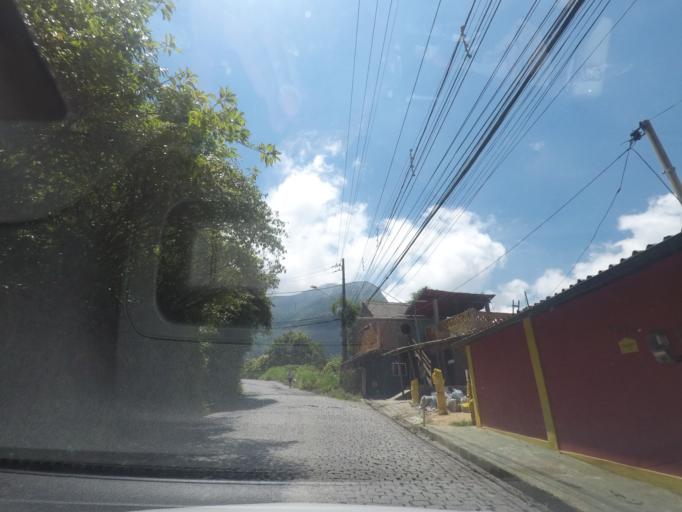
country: BR
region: Rio de Janeiro
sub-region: Petropolis
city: Petropolis
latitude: -22.5351
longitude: -43.1729
